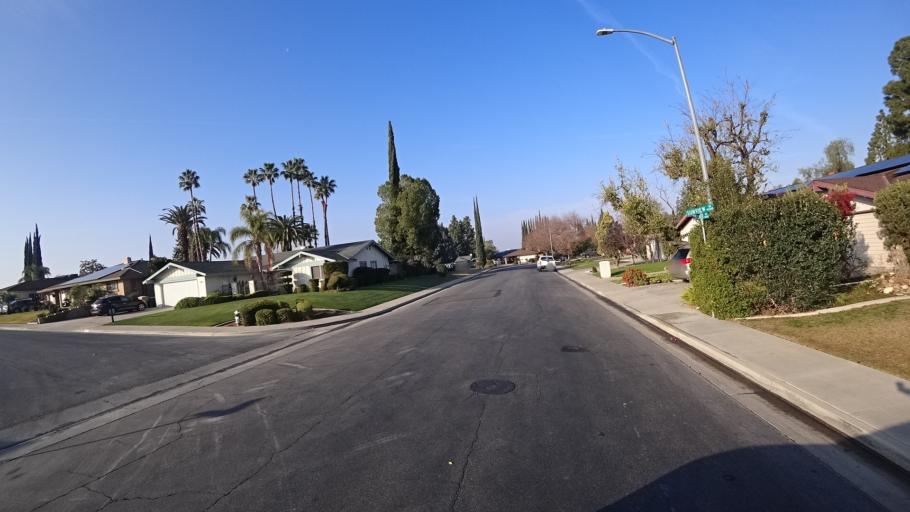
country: US
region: California
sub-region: Kern County
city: Oildale
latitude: 35.4034
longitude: -118.9431
